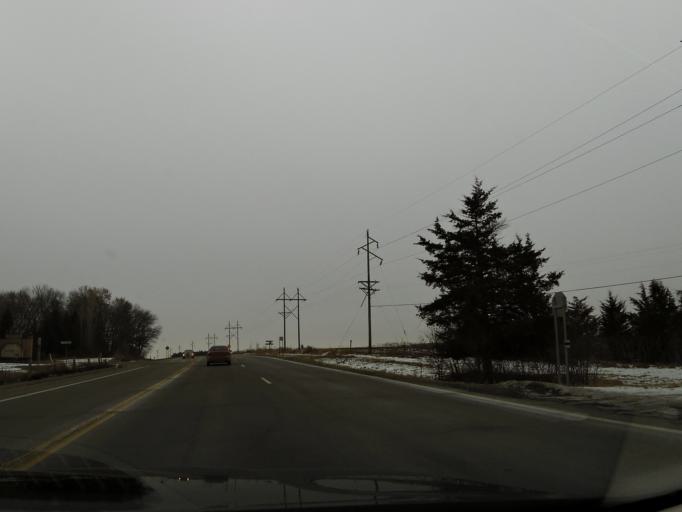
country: US
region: Minnesota
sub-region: Scott County
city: Jordan
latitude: 44.6501
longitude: -93.6281
